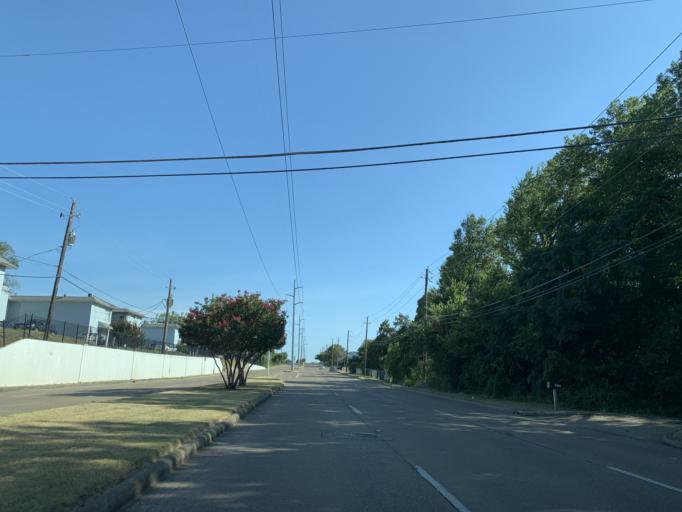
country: US
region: Texas
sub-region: Dallas County
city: Cockrell Hill
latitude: 32.6971
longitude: -96.8915
